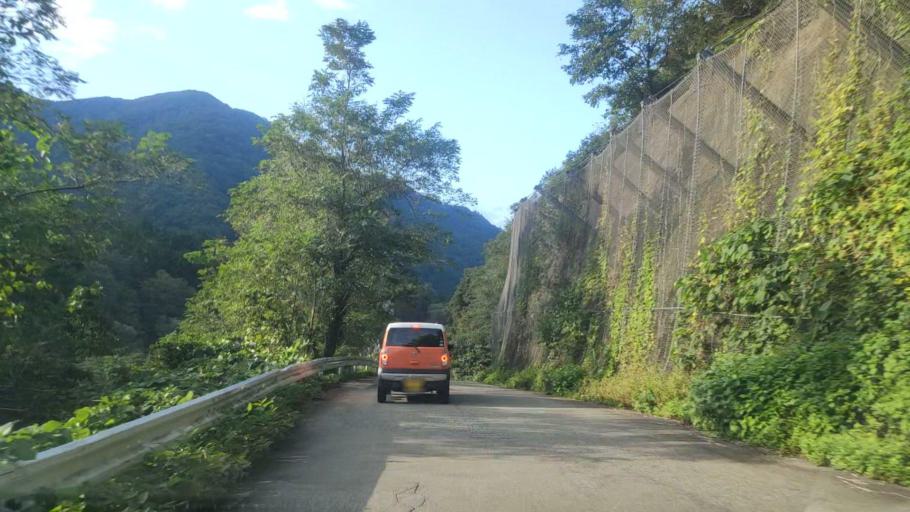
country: JP
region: Toyama
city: Yatsuomachi-higashikumisaka
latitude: 36.4521
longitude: 137.0849
